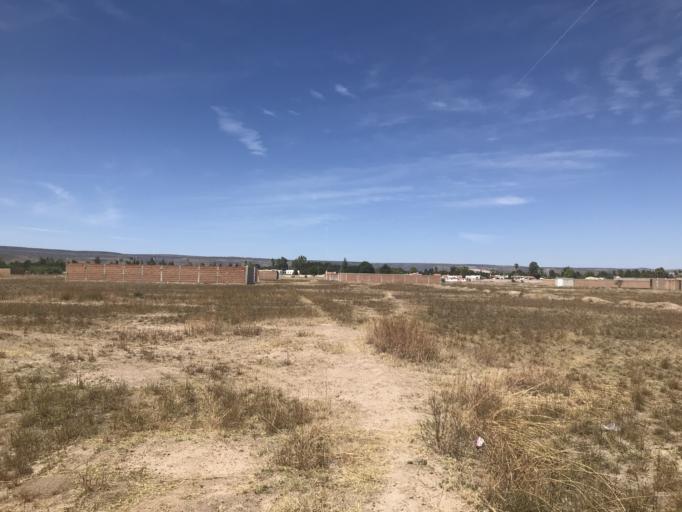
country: MX
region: Durango
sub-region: Durango
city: Sebastian Lerdo de Tejada
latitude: 23.9774
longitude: -104.6552
